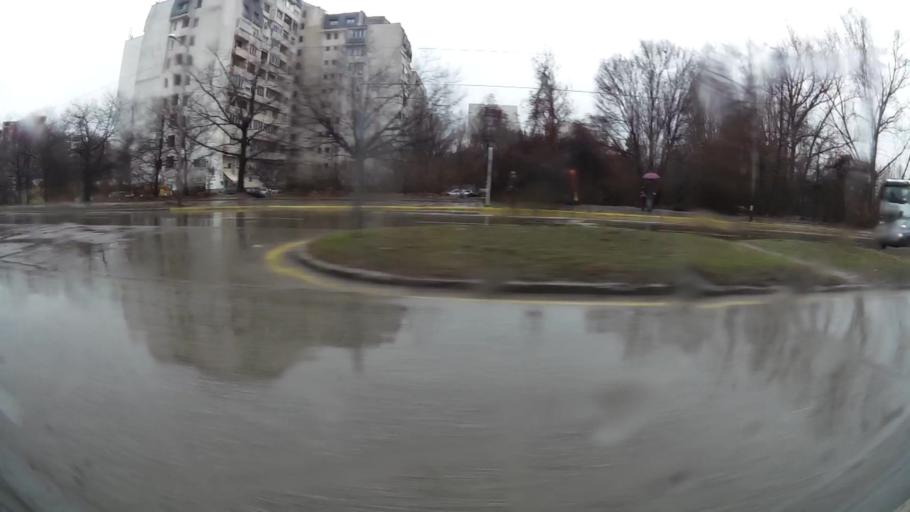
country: BG
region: Sofia-Capital
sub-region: Stolichna Obshtina
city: Sofia
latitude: 42.6515
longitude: 23.3562
